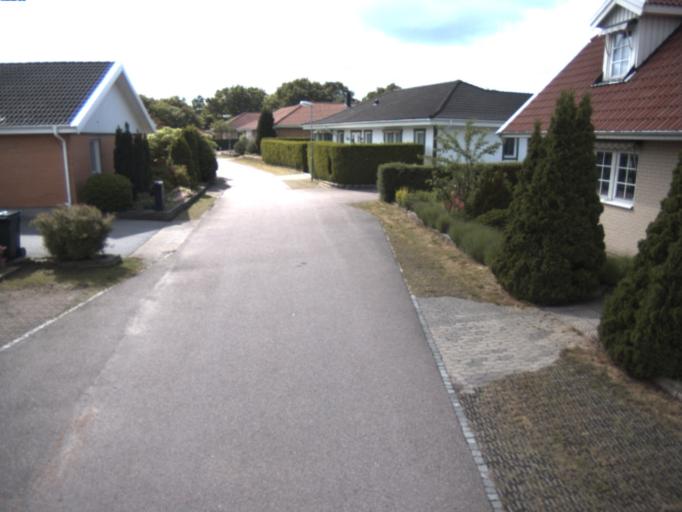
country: SE
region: Skane
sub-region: Helsingborg
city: Helsingborg
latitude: 56.0322
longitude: 12.7484
